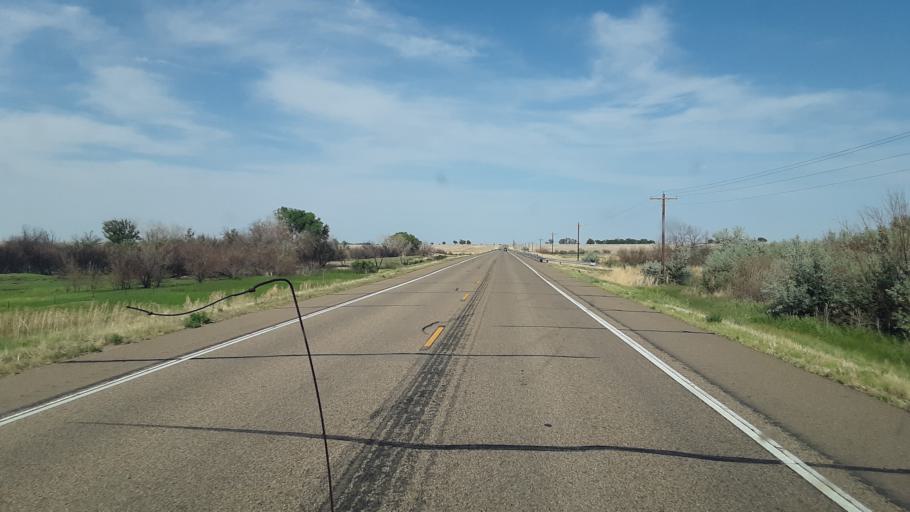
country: US
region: Colorado
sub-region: Bent County
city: Las Animas
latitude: 38.1132
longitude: -103.0830
